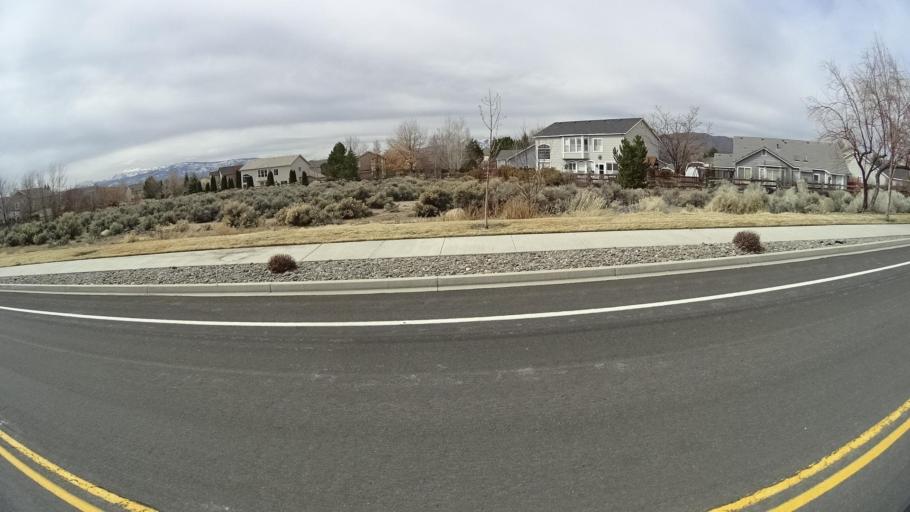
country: US
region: Nevada
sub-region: Washoe County
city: Spanish Springs
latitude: 39.6296
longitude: -119.6807
